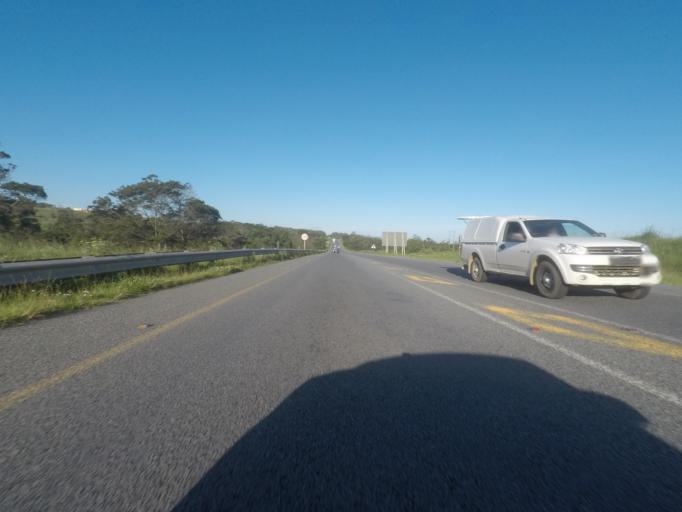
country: ZA
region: Eastern Cape
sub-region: Buffalo City Metropolitan Municipality
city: East London
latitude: -33.0514
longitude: 27.8113
